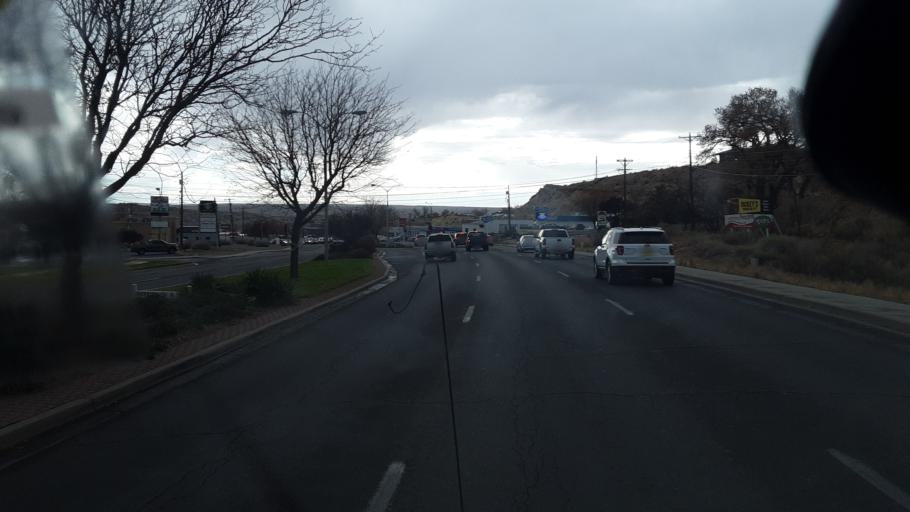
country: US
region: New Mexico
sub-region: San Juan County
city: Farmington
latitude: 36.7633
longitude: -108.1547
